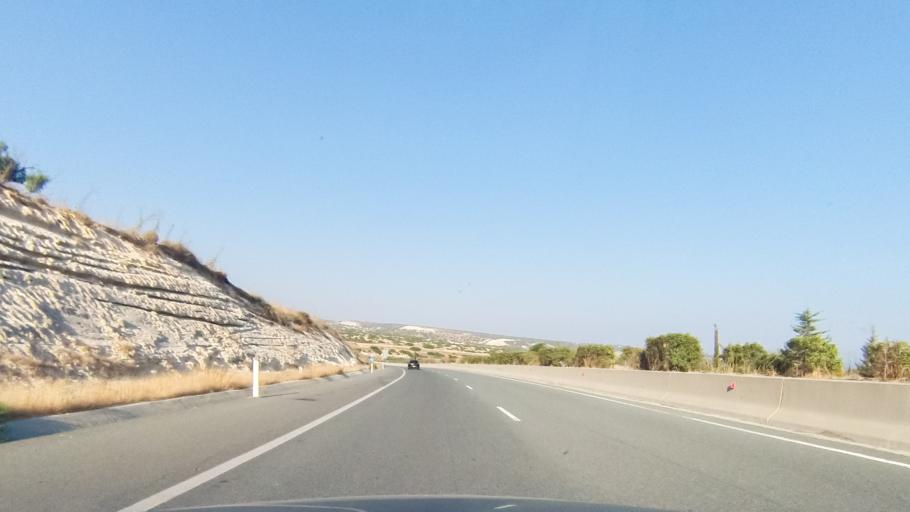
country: CY
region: Limassol
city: Pissouri
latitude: 34.6823
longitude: 32.7658
